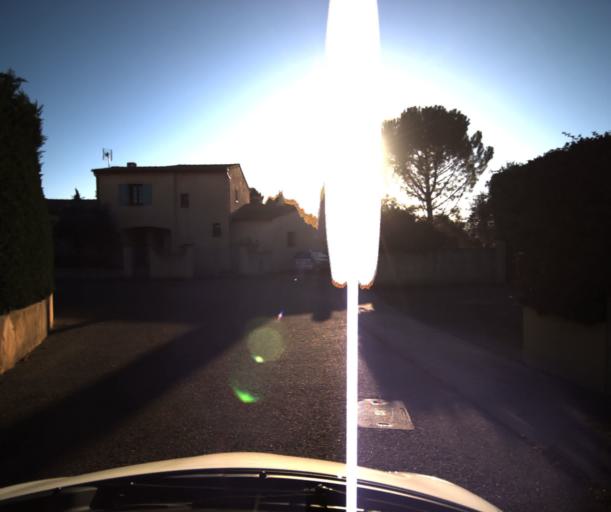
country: FR
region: Provence-Alpes-Cote d'Azur
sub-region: Departement du Vaucluse
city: Pertuis
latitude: 43.6876
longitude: 5.5065
